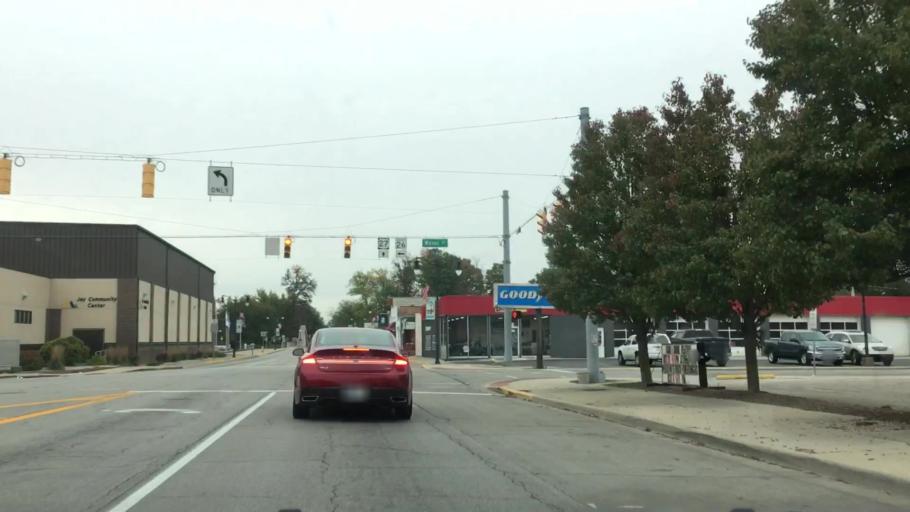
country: US
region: Indiana
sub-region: Jay County
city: Portland
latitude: 40.4326
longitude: -84.9779
